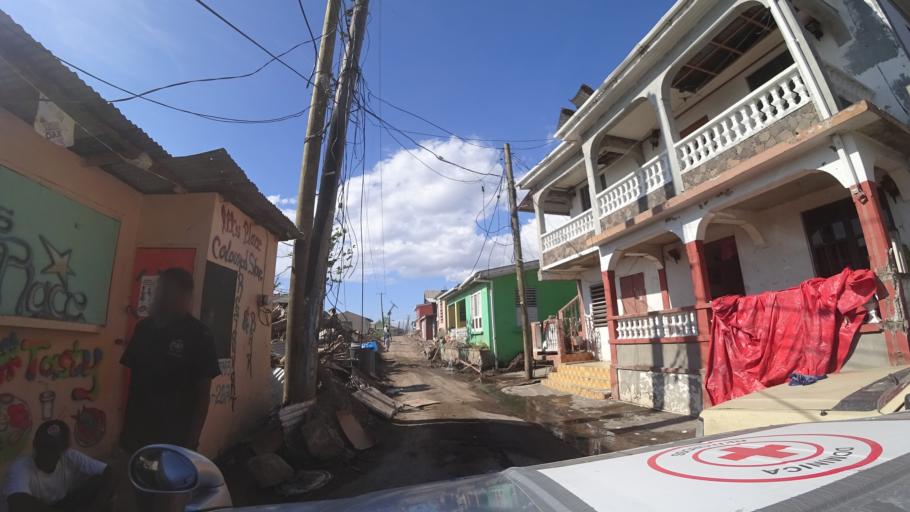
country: DM
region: Saint Luke
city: Pointe Michel
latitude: 15.2573
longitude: -61.3768
